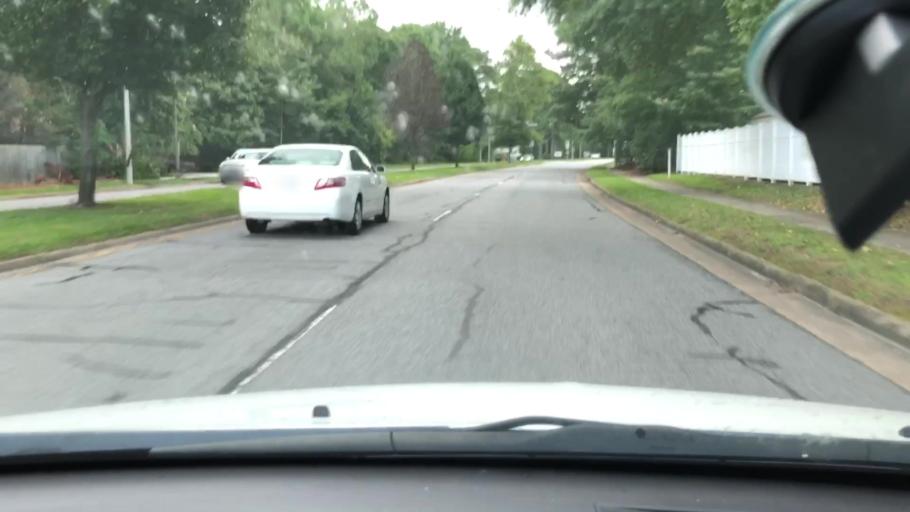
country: US
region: Virginia
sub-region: City of Chesapeake
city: Chesapeake
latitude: 36.8152
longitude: -76.1772
